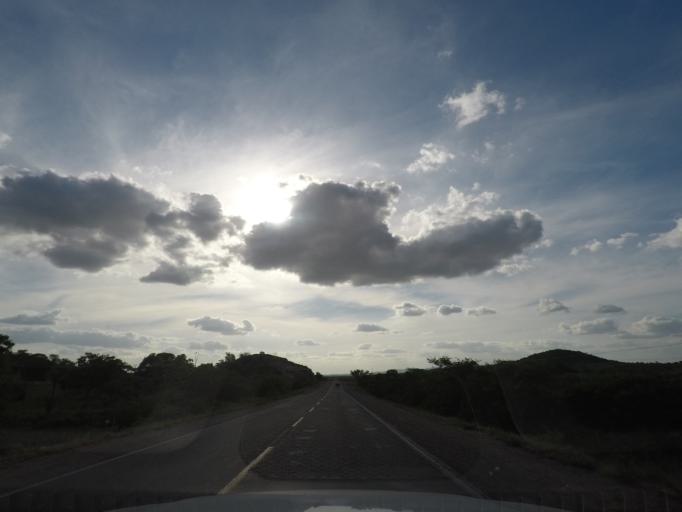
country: BR
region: Bahia
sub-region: Anguera
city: Anguera
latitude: -12.1836
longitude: -39.4690
